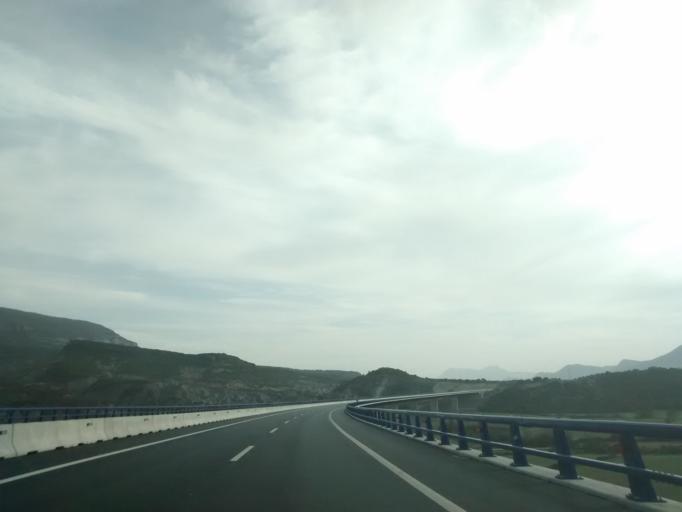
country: ES
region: Aragon
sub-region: Provincia de Zaragoza
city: Siguees
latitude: 42.6260
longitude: -1.0182
